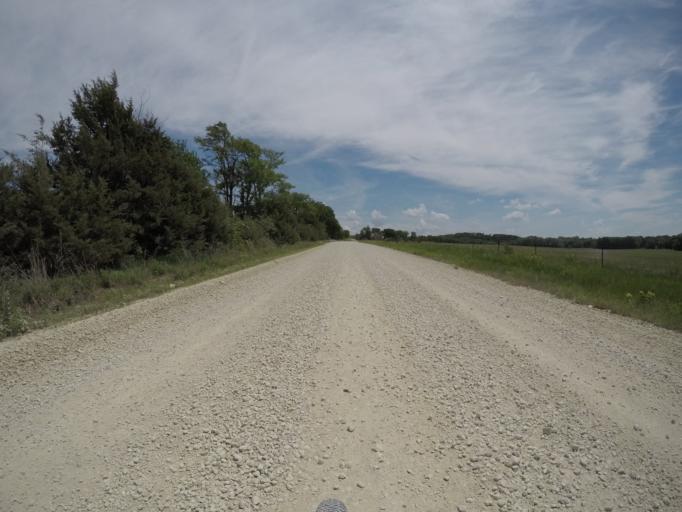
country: US
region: Kansas
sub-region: Wabaunsee County
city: Alma
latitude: 38.9646
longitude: -96.2554
